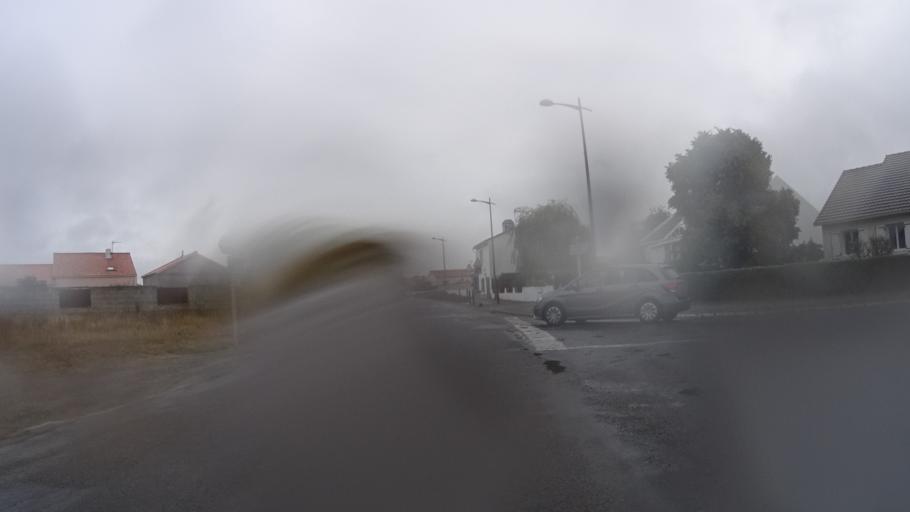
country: FR
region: Pays de la Loire
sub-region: Departement de la Loire-Atlantique
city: Corsept
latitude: 47.2745
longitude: -2.0619
